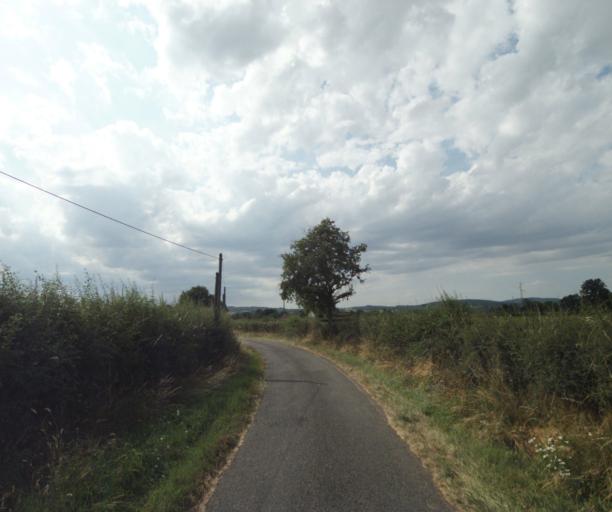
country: FR
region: Bourgogne
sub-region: Departement de Saone-et-Loire
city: Gueugnon
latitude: 46.6125
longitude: 4.0792
